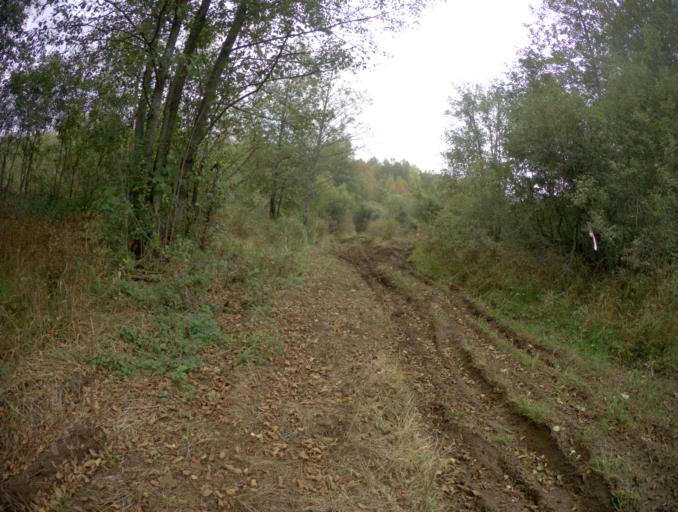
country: RU
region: Moskovskaya
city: Misheronskiy
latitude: 55.7754
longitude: 39.6038
